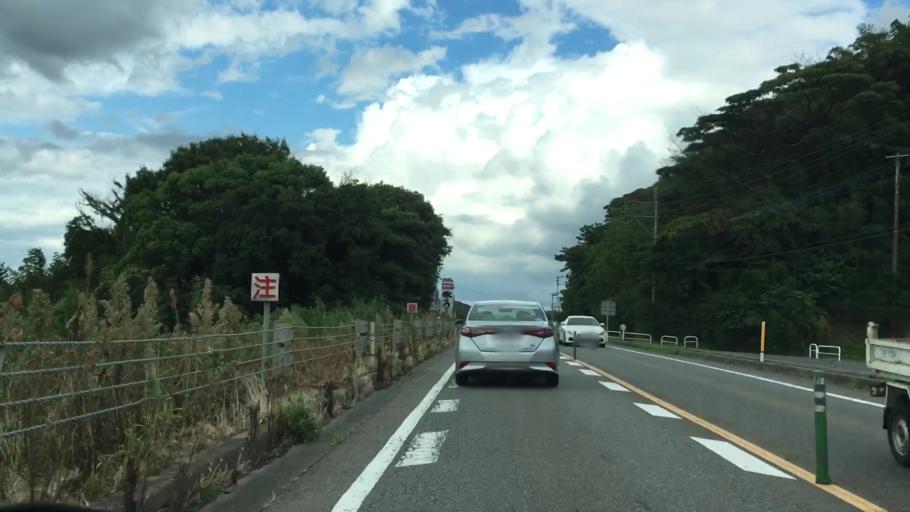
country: JP
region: Fukuoka
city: Maebaru-chuo
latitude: 33.5079
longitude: 130.1235
